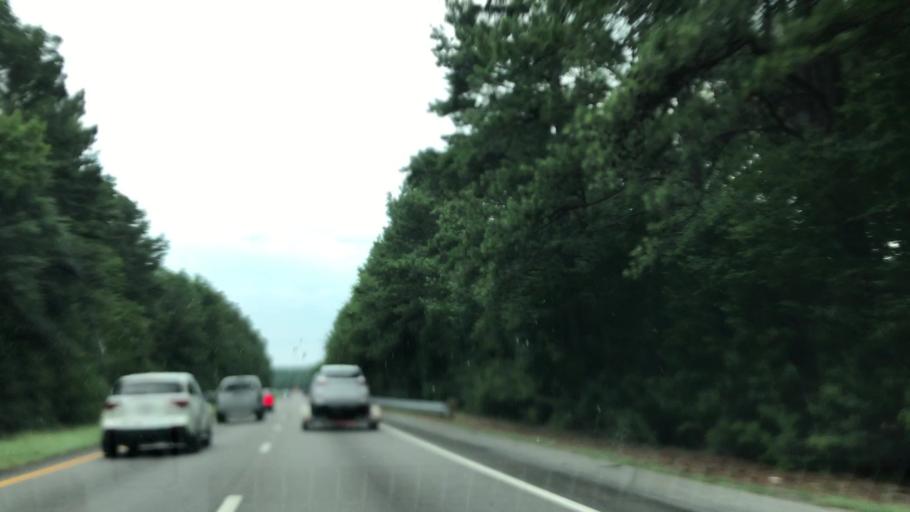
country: US
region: South Carolina
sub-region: Richland County
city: Blythewood
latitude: 34.2521
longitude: -80.9996
